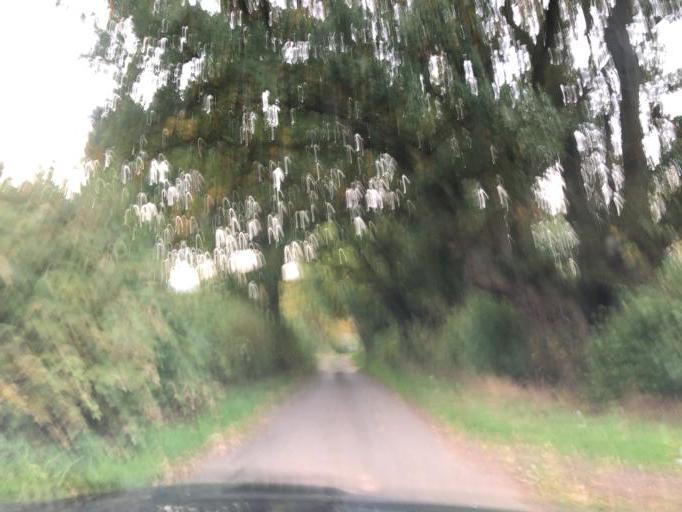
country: GB
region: England
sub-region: Warwickshire
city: Wroxall
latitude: 52.3151
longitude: -1.6569
